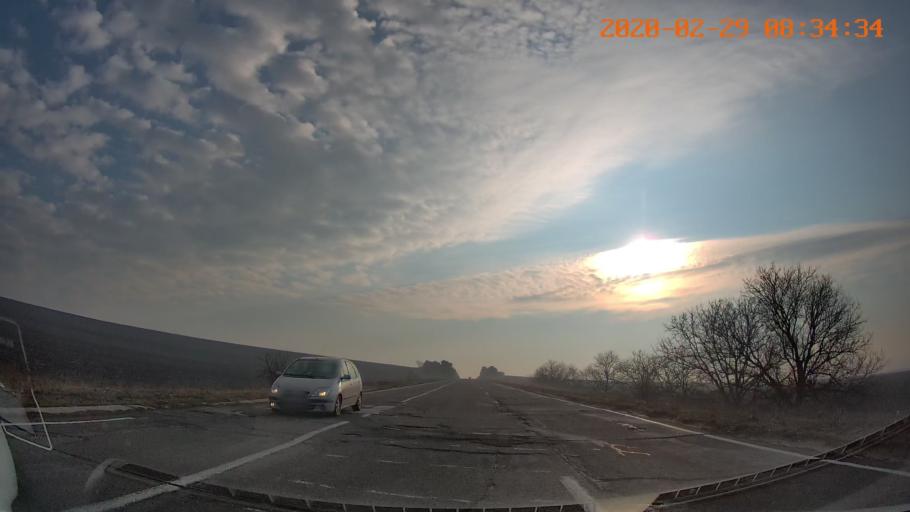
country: MD
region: Anenii Noi
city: Anenii Noi
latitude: 46.9246
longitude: 29.3115
